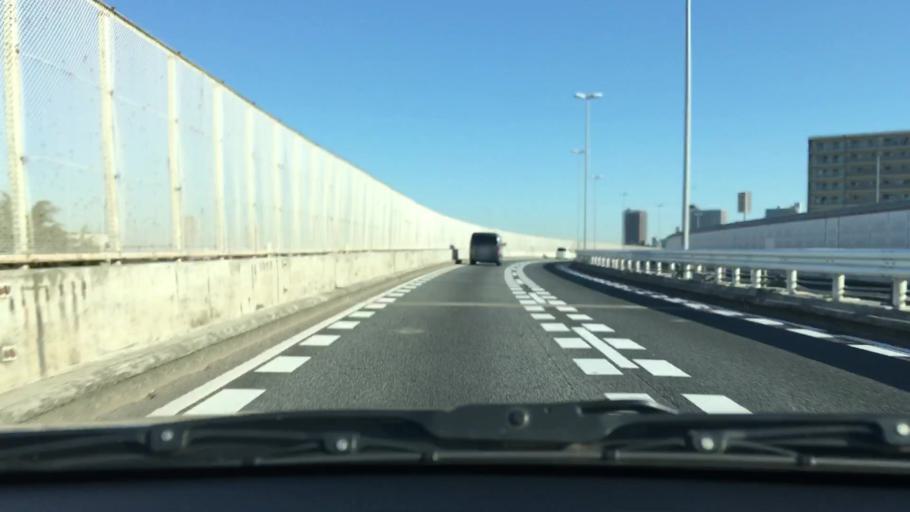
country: JP
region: Tokyo
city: Urayasu
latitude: 35.7002
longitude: 139.8957
